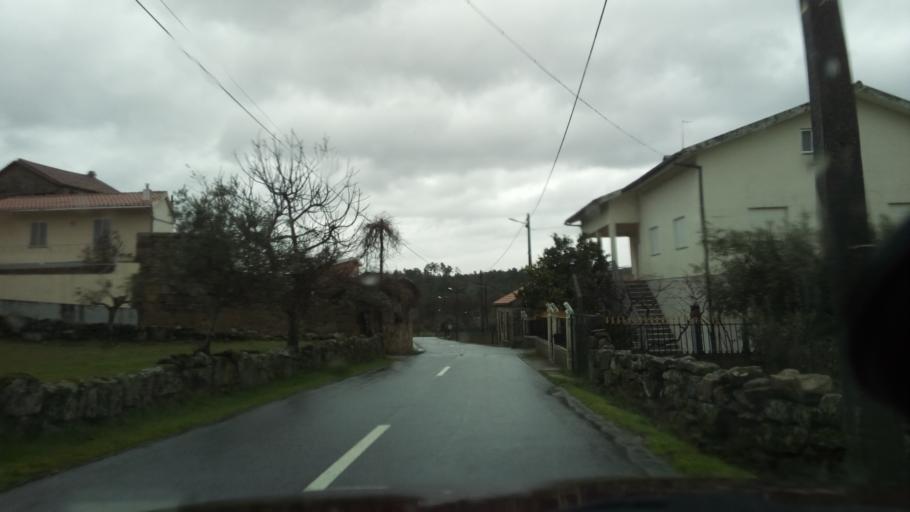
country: PT
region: Guarda
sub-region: Fornos de Algodres
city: Fornos de Algodres
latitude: 40.5848
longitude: -7.5115
